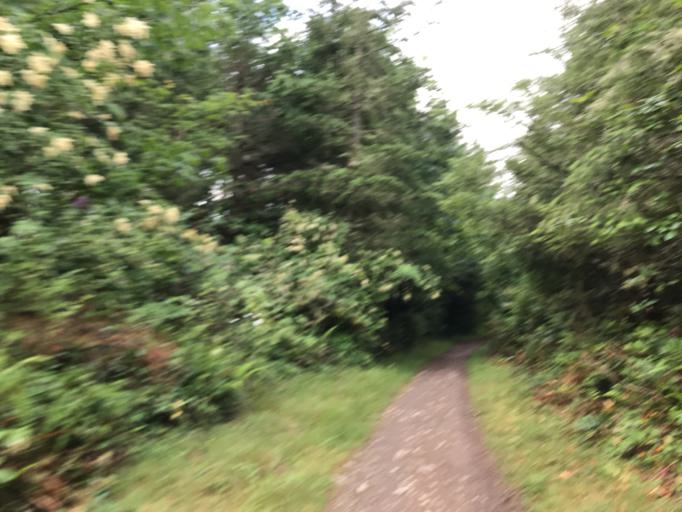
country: US
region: Washington
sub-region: King County
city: Ravensdale
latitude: 47.3404
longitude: -122.0056
